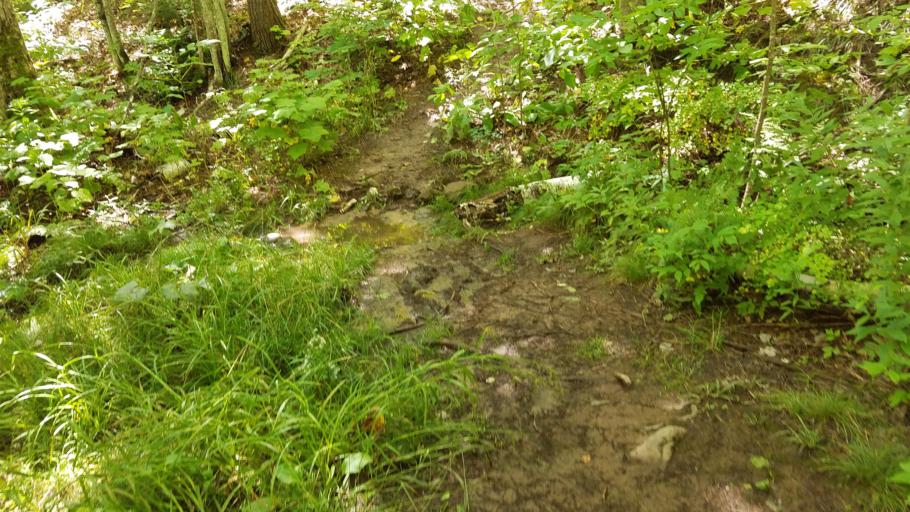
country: US
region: Michigan
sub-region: Ontonagon County
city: Ontonagon
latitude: 46.6511
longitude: -89.1533
